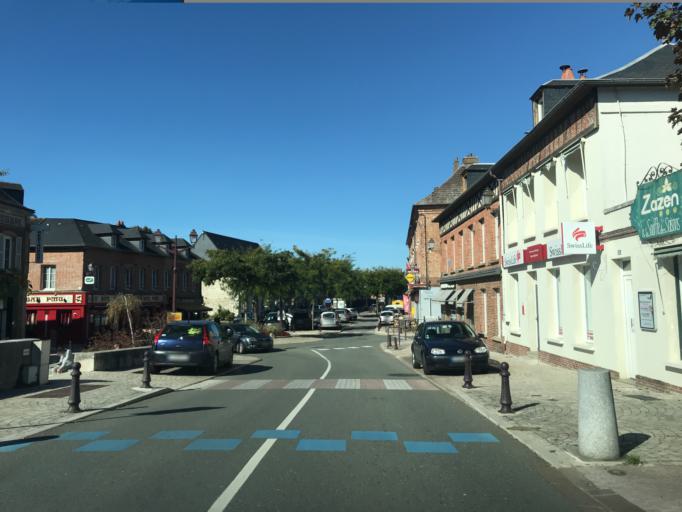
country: FR
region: Haute-Normandie
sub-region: Departement de l'Eure
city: Le Vaudreuil
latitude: 49.2559
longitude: 1.2095
